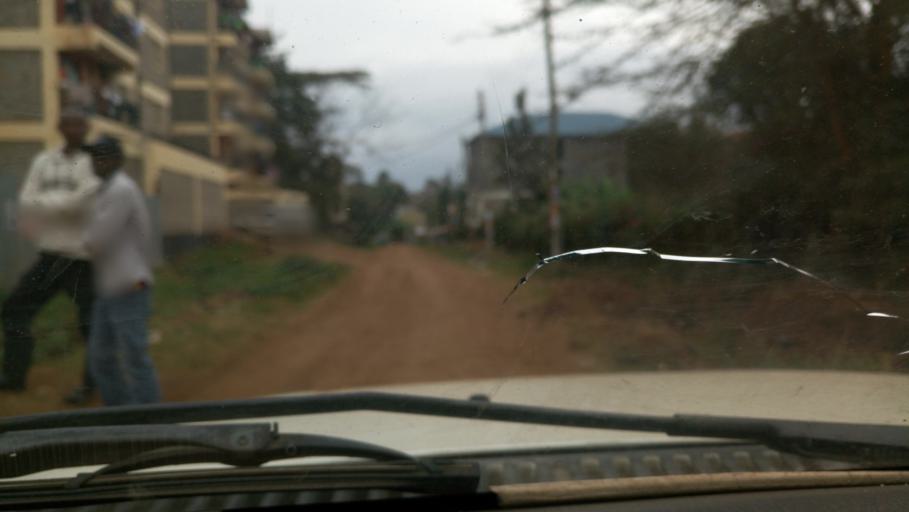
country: KE
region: Kiambu
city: Kiambu
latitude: -1.1891
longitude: 36.8982
